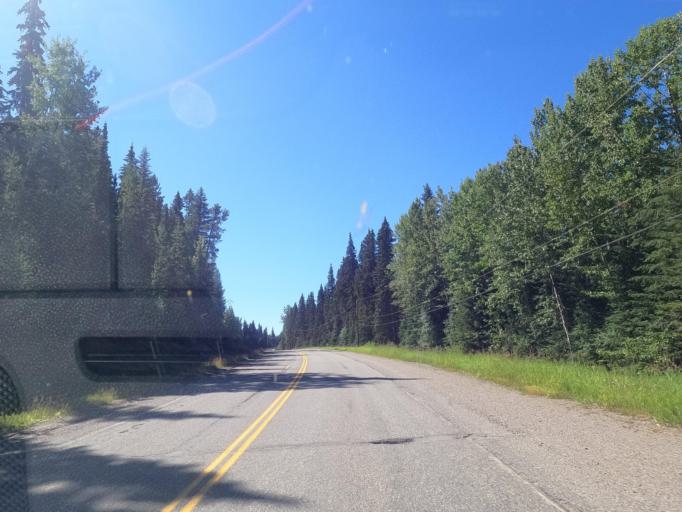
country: CA
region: British Columbia
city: Quesnel
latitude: 53.0391
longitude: -122.2609
